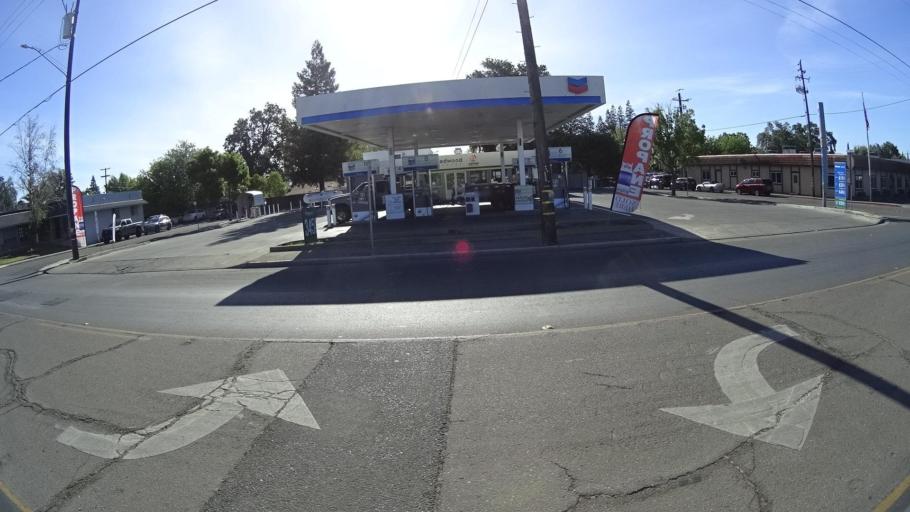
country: US
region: California
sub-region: Lake County
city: Lakeport
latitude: 39.0350
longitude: -122.9157
